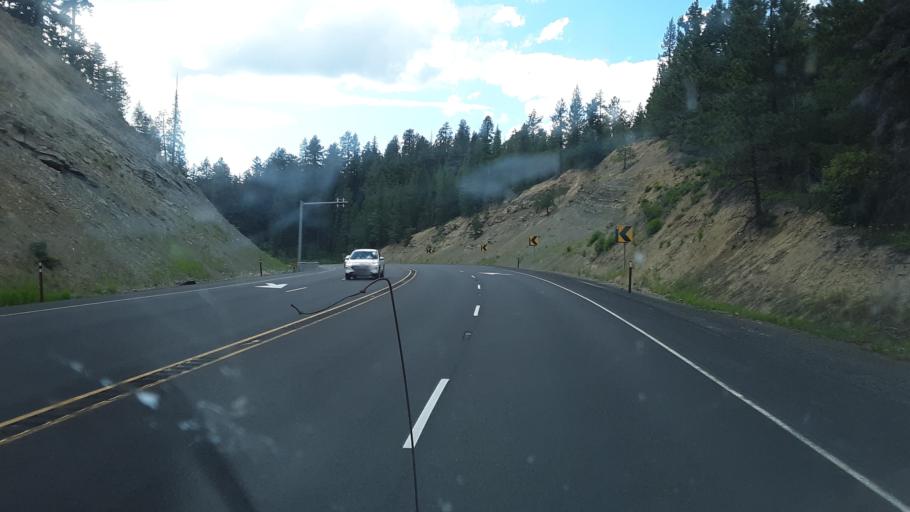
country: US
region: Washington
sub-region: Chelan County
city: Cashmere
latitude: 47.3346
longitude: -120.5776
